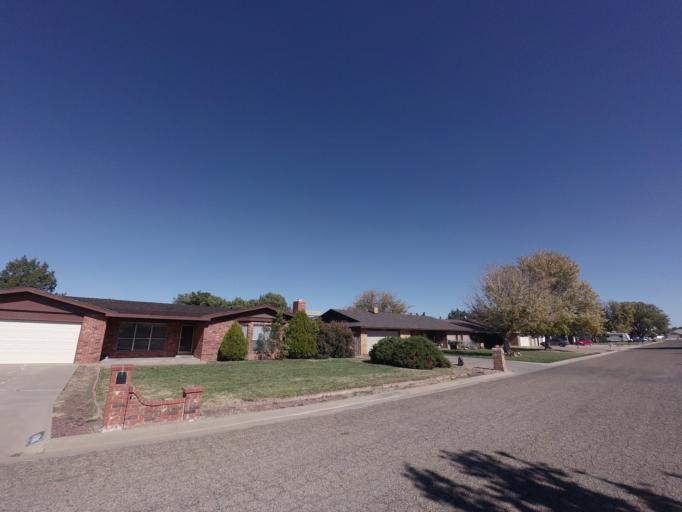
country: US
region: New Mexico
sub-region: Curry County
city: Clovis
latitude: 34.4225
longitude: -103.1923
